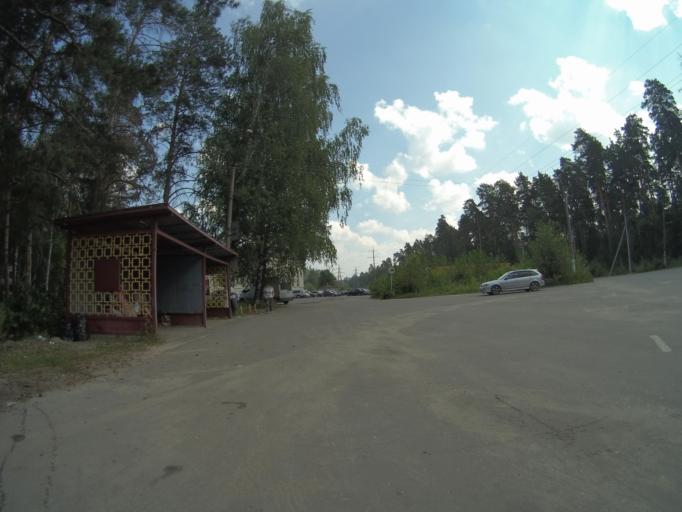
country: RU
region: Vladimir
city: Gus'-Khrustal'nyy
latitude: 55.6327
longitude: 40.6946
